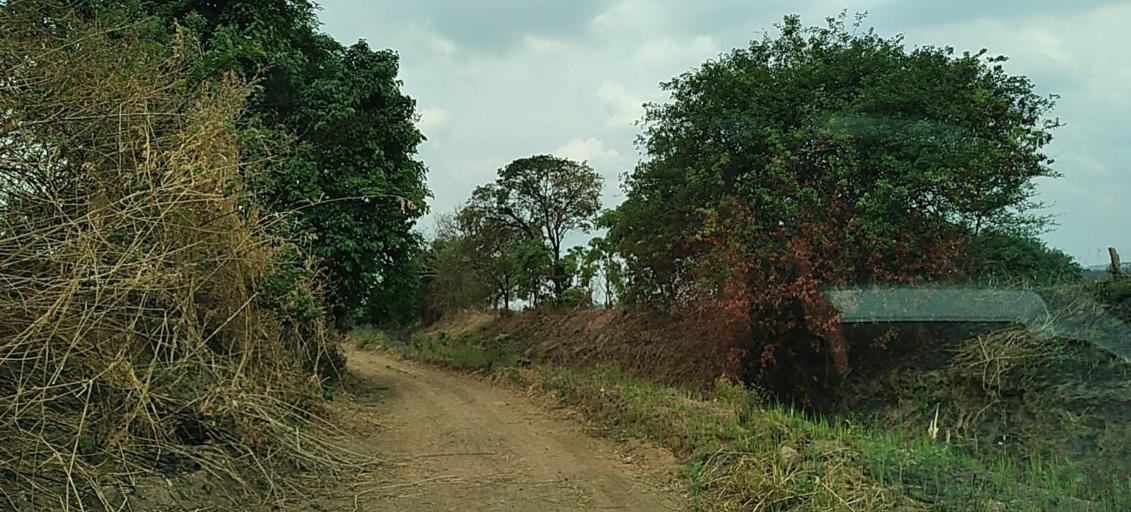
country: ZM
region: Copperbelt
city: Chililabombwe
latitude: -12.3608
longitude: 27.8009
